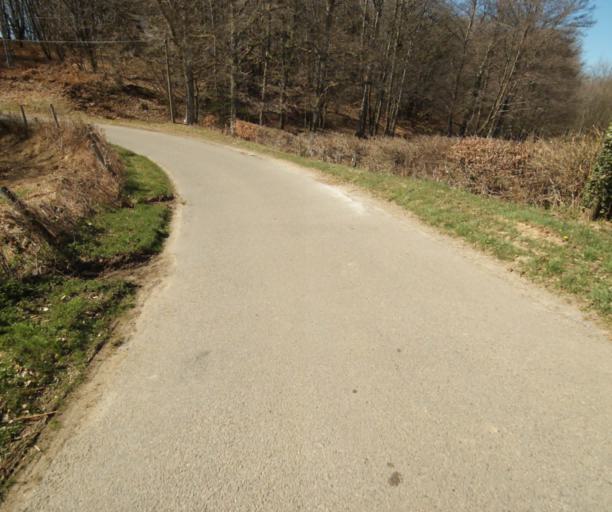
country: FR
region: Limousin
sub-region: Departement de la Correze
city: Saint-Clement
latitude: 45.3064
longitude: 1.7068
